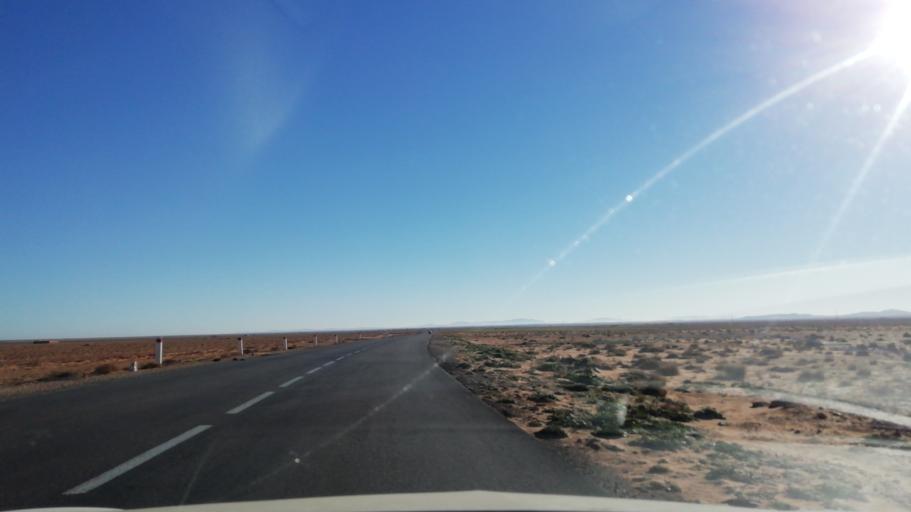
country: DZ
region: El Bayadh
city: El Bayadh
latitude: 33.8603
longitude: 0.5549
